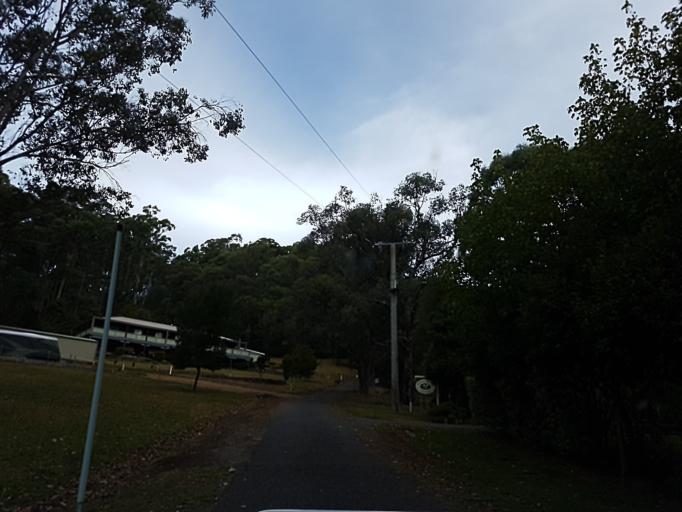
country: AU
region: Victoria
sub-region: Alpine
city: Mount Beauty
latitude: -36.8998
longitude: 147.0589
